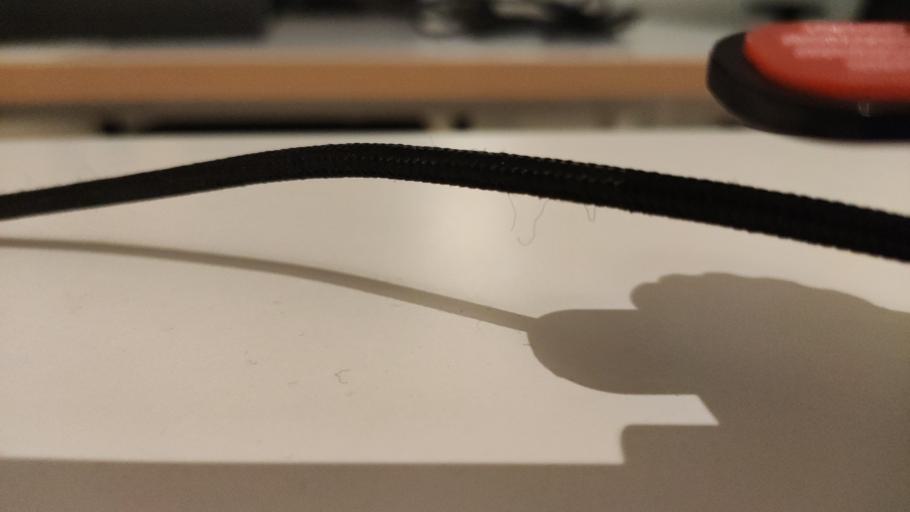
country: RU
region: Moskovskaya
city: Kurovskoye
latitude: 55.5904
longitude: 38.9207
